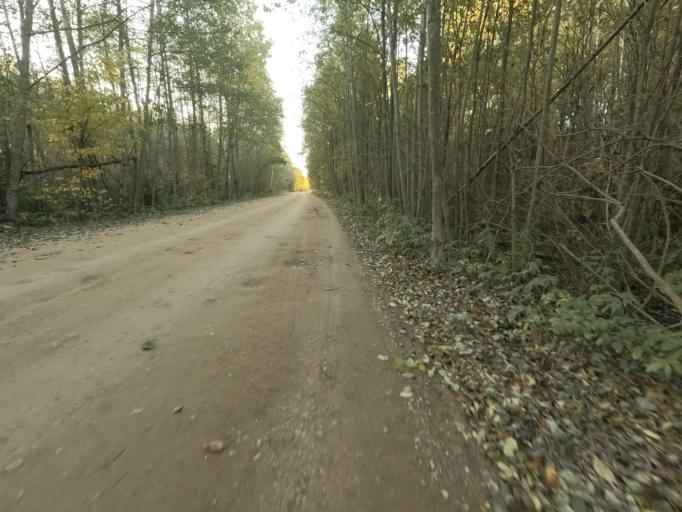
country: RU
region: Leningrad
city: Lyuban'
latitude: 58.9977
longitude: 31.1043
